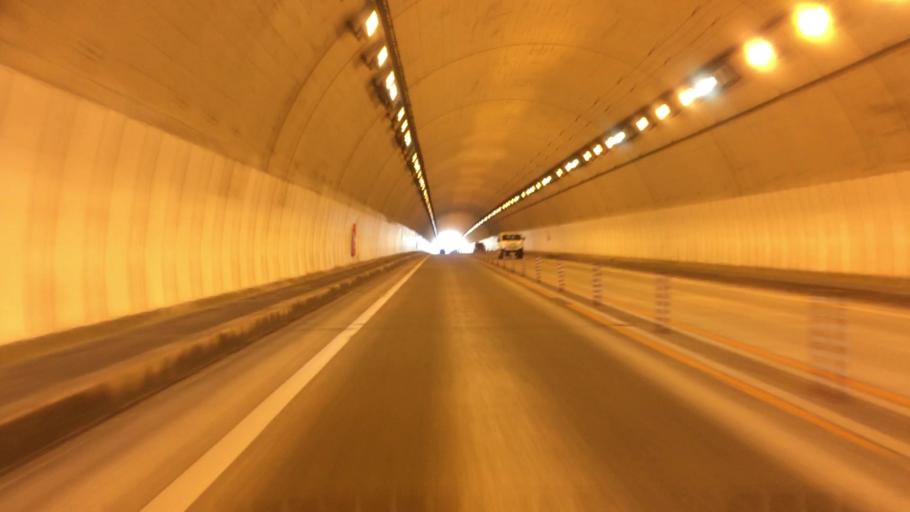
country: JP
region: Kyoto
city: Fukuchiyama
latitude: 35.2287
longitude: 135.0262
